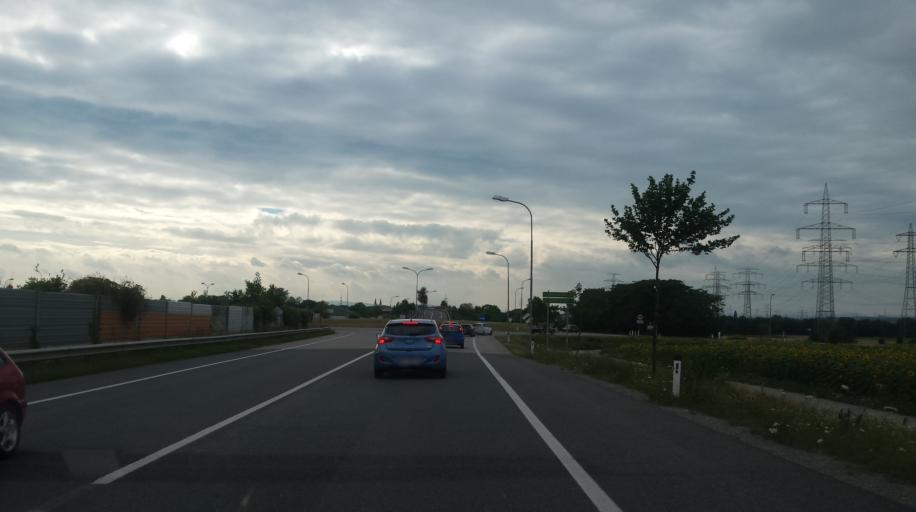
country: AT
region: Lower Austria
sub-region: Politischer Bezirk Wien-Umgebung
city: Himberg
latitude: 48.0916
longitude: 16.4485
